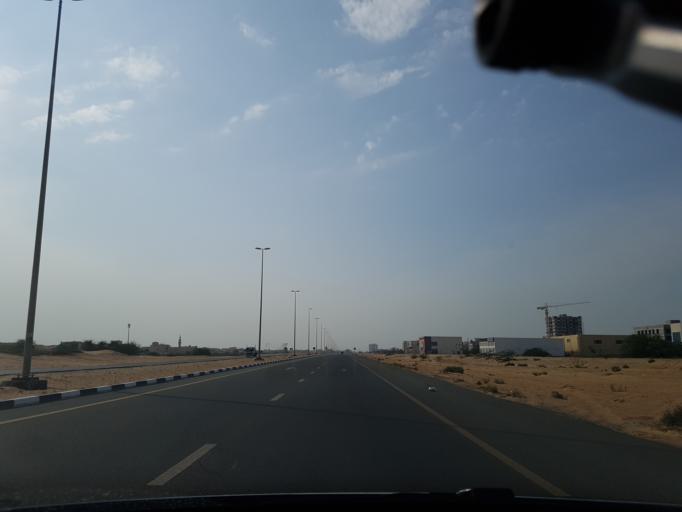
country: AE
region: Ajman
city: Ajman
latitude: 25.4175
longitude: 55.5452
